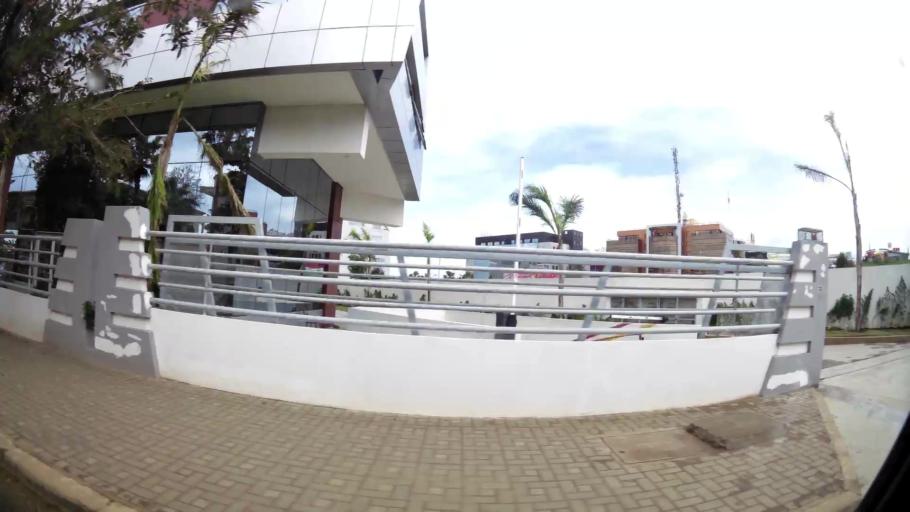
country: MA
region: Grand Casablanca
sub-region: Casablanca
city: Casablanca
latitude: 33.5388
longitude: -7.6441
